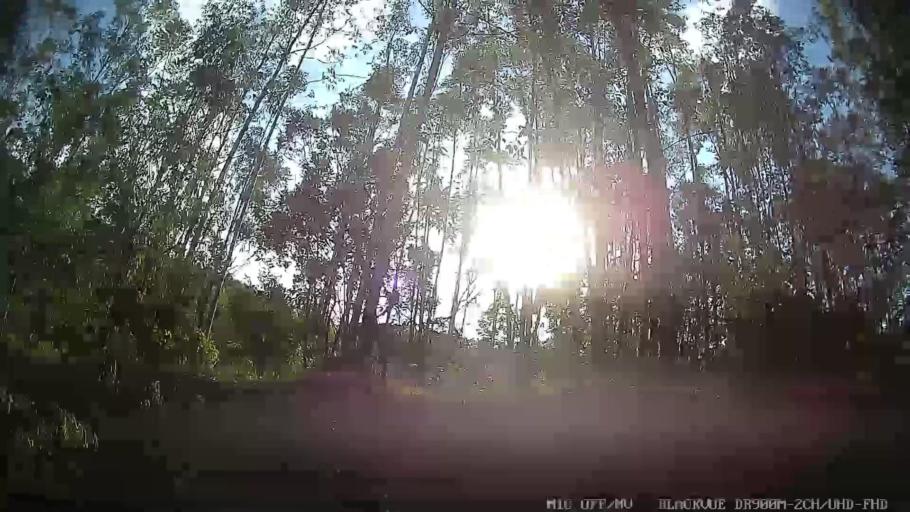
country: BR
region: Sao Paulo
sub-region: Serra Negra
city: Serra Negra
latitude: -22.6615
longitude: -46.6895
